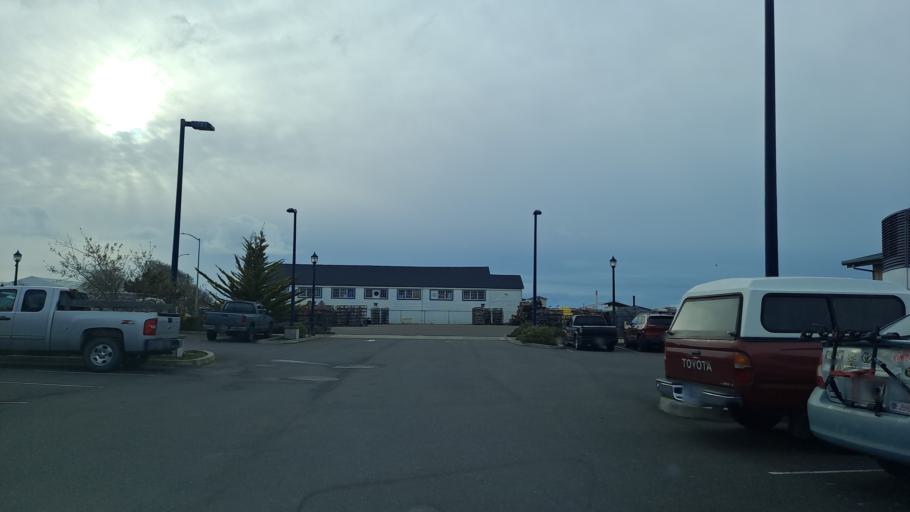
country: US
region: California
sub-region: Humboldt County
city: Eureka
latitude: 40.8051
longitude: -124.1704
